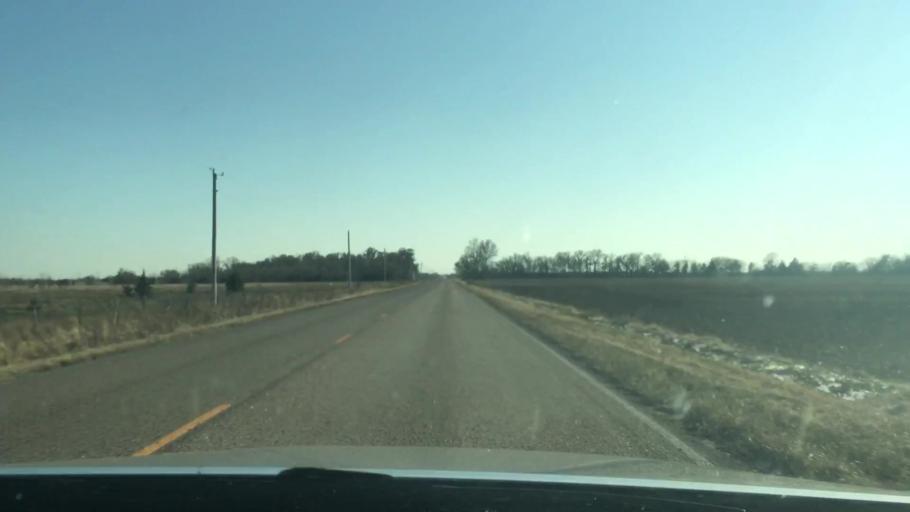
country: US
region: Kansas
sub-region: Reno County
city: Nickerson
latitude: 38.1859
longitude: -98.0876
